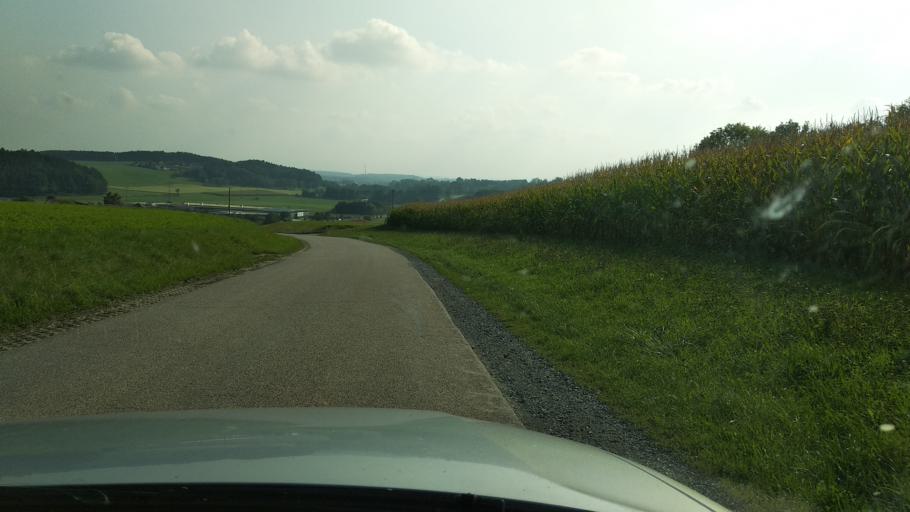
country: DE
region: Bavaria
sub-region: Upper Bavaria
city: Ebersberg
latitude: 48.0860
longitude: 11.9866
